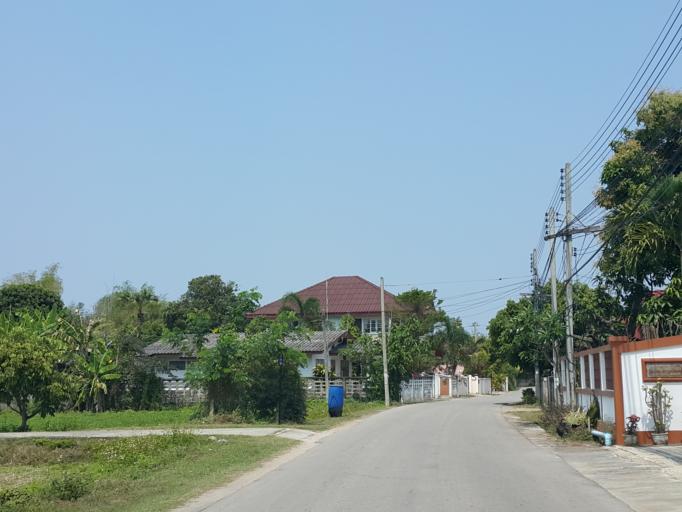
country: TH
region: Lampang
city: Lampang
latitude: 18.3075
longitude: 99.4395
